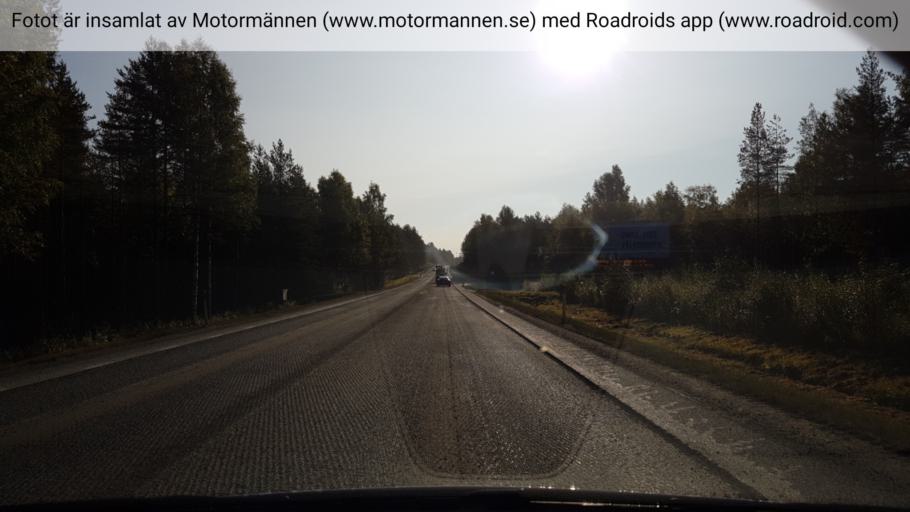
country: SE
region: Vaesterbotten
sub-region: Umea Kommun
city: Roback
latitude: 63.8441
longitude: 20.1700
